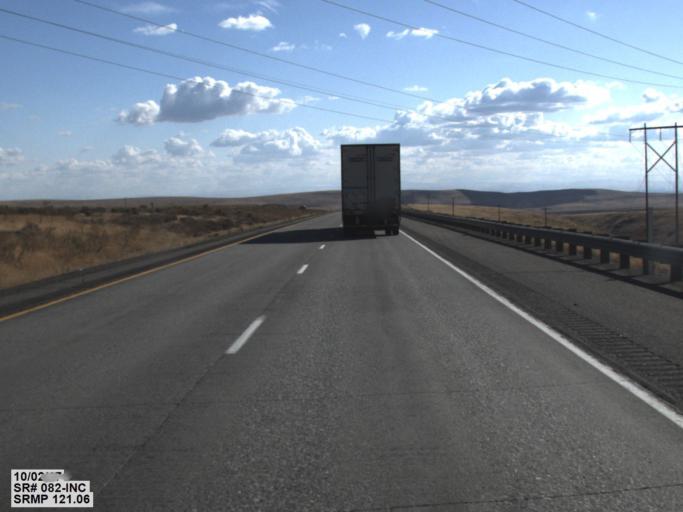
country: US
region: Washington
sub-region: Benton County
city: Highland
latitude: 46.0498
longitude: -119.2245
